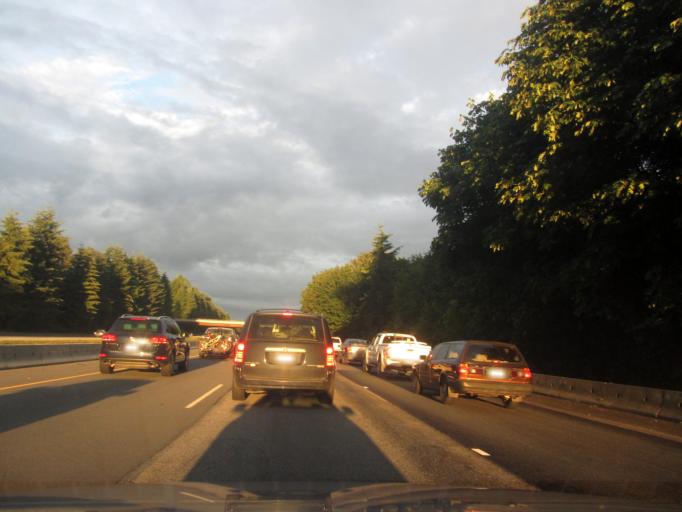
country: CA
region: British Columbia
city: Langley
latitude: 49.1202
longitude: -122.5408
